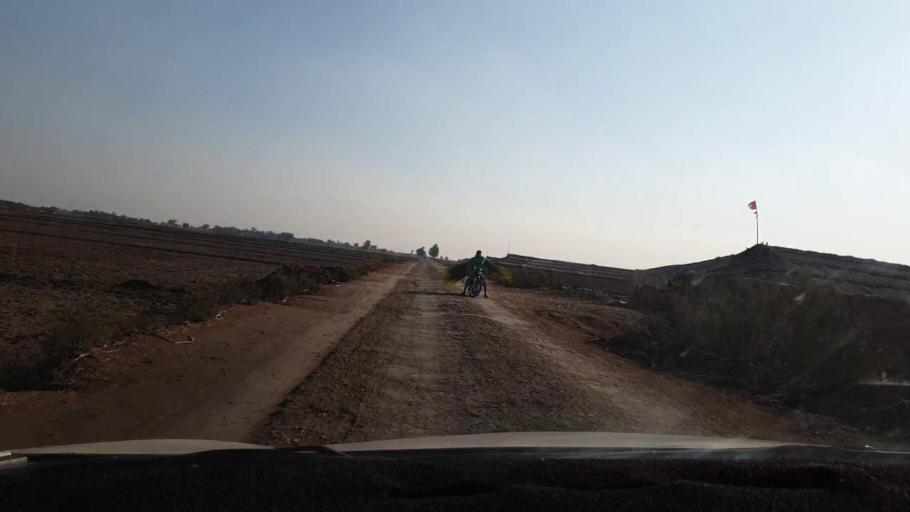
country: PK
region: Sindh
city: Berani
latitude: 25.7723
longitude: 68.7686
